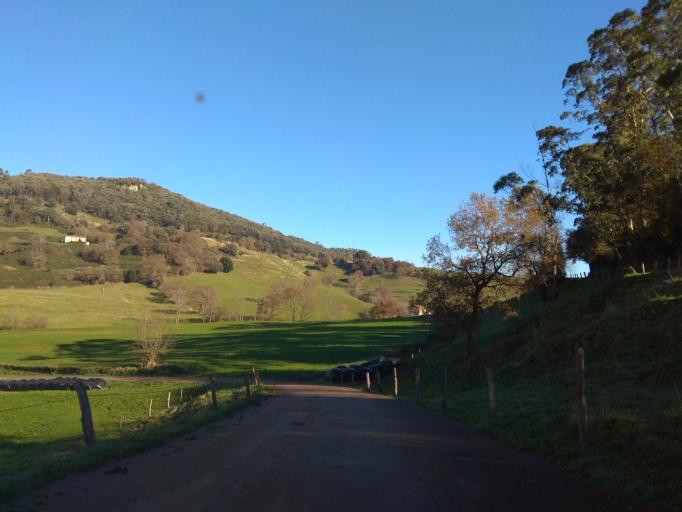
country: ES
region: Cantabria
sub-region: Provincia de Cantabria
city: Entrambasaguas
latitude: 43.3718
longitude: -3.7077
